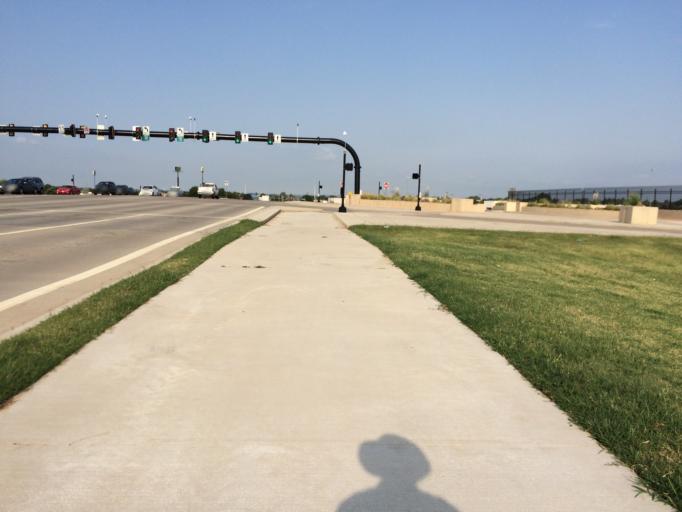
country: US
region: Oklahoma
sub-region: Cleveland County
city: Norman
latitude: 35.2186
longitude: -97.4847
